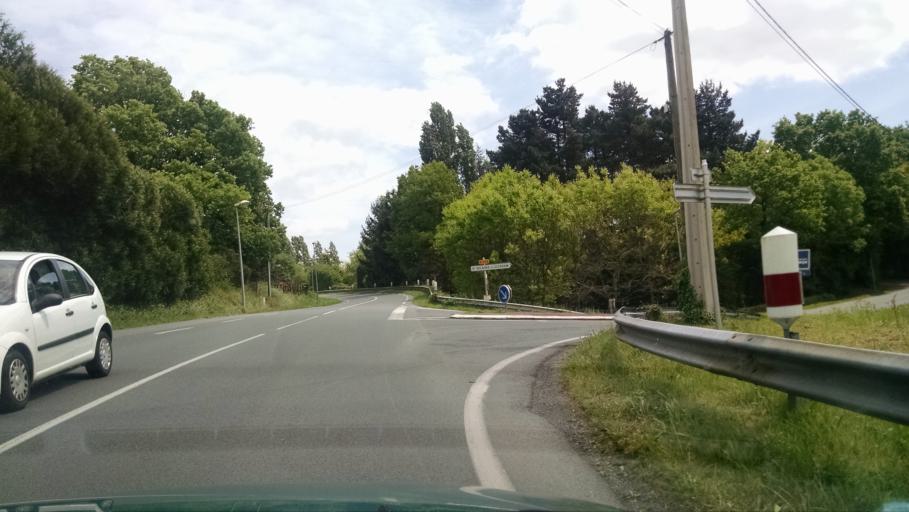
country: FR
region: Pays de la Loire
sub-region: Departement de la Loire-Atlantique
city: Gorges
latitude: 47.0932
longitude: -1.3106
